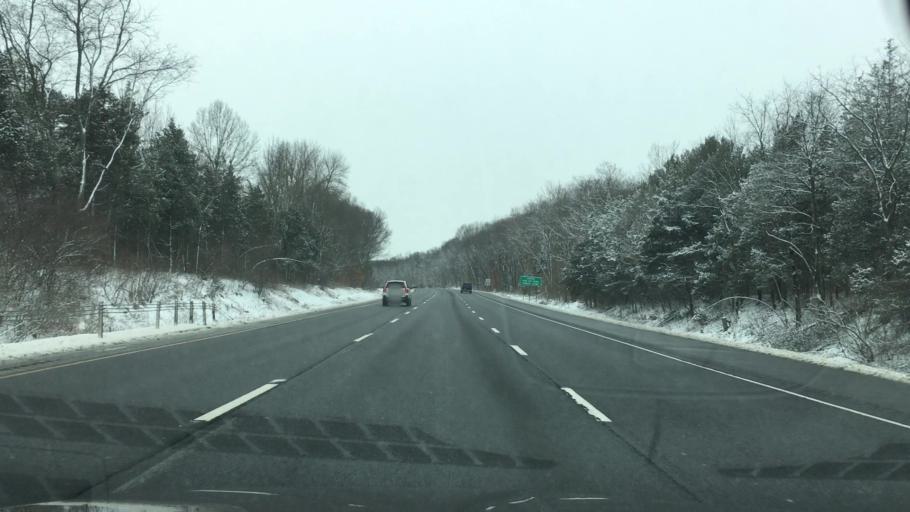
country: US
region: Connecticut
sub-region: Middlesex County
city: Cromwell
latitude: 41.6016
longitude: -72.7063
